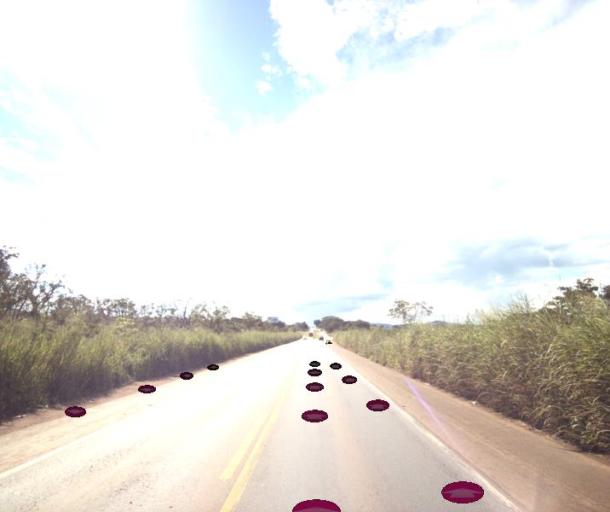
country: BR
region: Goias
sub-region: Jaragua
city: Jaragua
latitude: -15.7625
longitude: -49.3117
